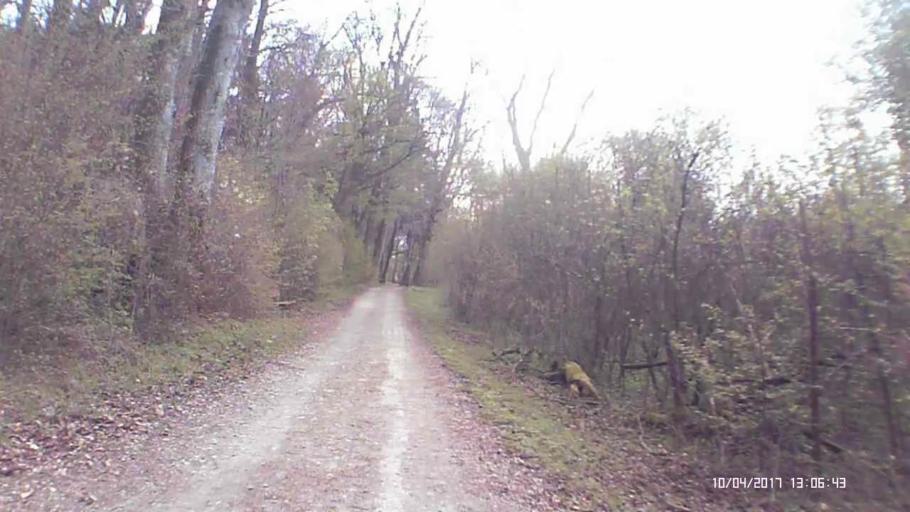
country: DE
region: Bavaria
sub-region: Upper Bavaria
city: Chieming
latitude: 47.9169
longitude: 12.4957
